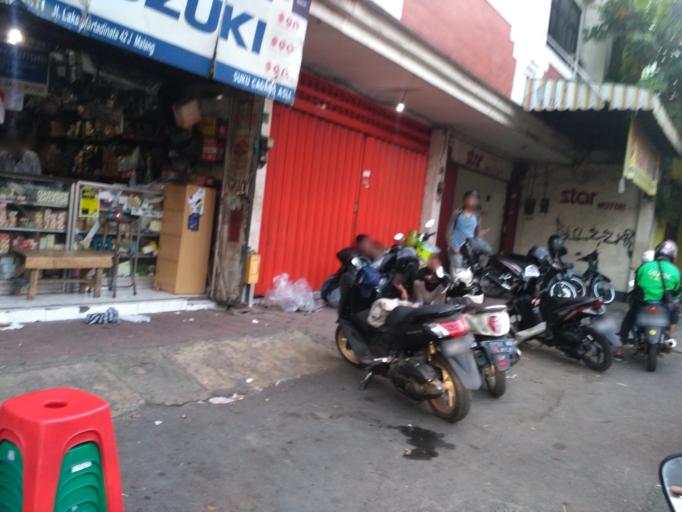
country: ID
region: East Java
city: Malang
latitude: -7.9920
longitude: 112.6340
